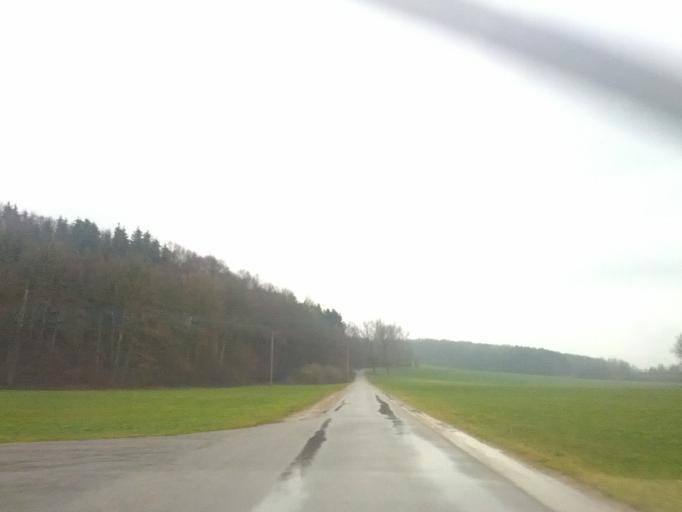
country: DE
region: Baden-Wuerttemberg
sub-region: Tuebingen Region
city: Rot an der Rot
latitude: 47.9954
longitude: 10.0005
